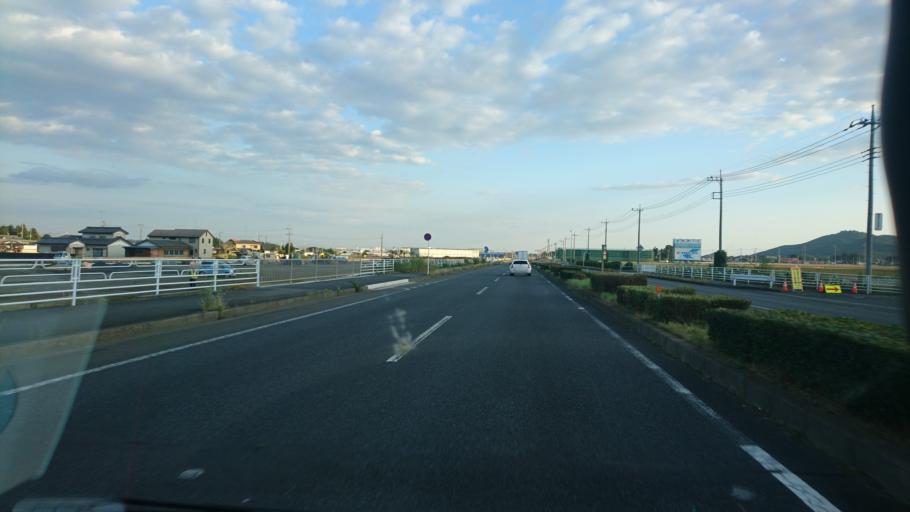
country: JP
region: Gunma
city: Ota
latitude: 36.3540
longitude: 139.3761
